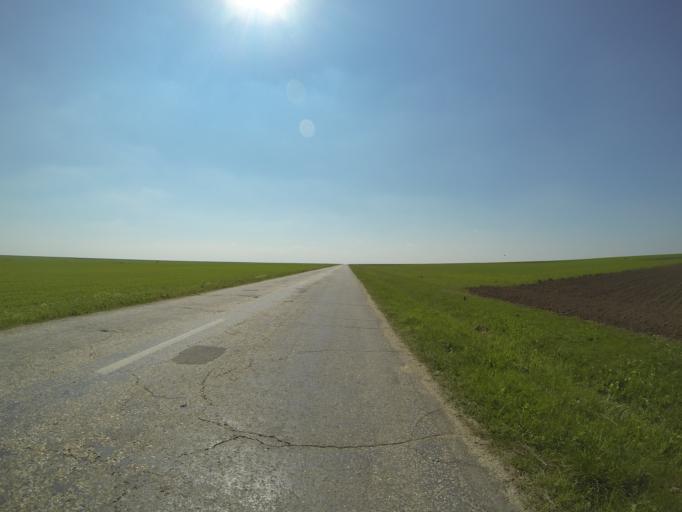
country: RO
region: Dolj
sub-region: Comuna Caraula
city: Caraula
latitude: 44.1849
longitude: 23.2295
